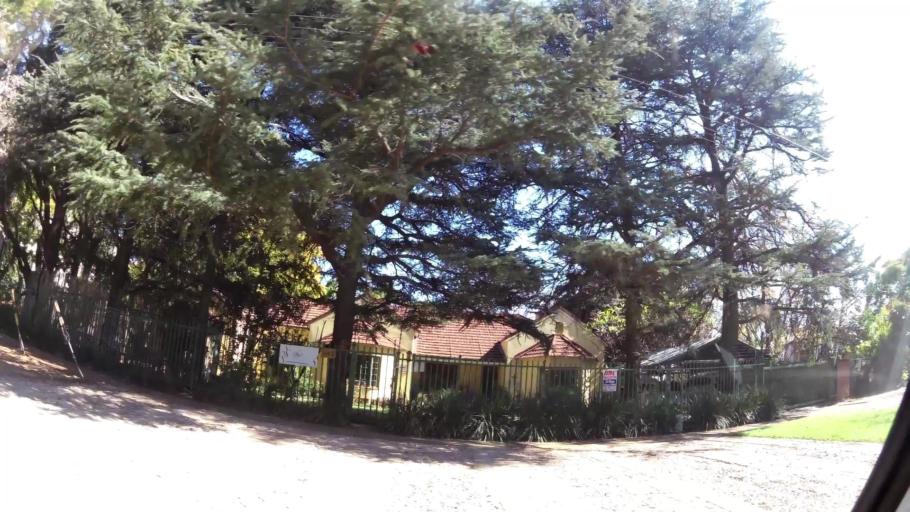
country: ZA
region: Gauteng
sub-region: City of Tshwane Metropolitan Municipality
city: Pretoria
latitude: -25.7469
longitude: 28.2422
